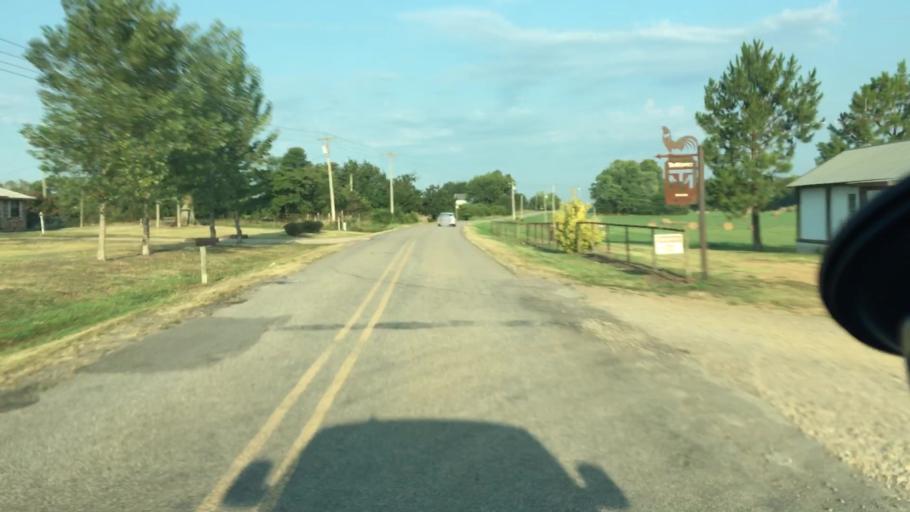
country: US
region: Arkansas
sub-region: Johnson County
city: Coal Hill
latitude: 35.3715
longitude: -93.5771
